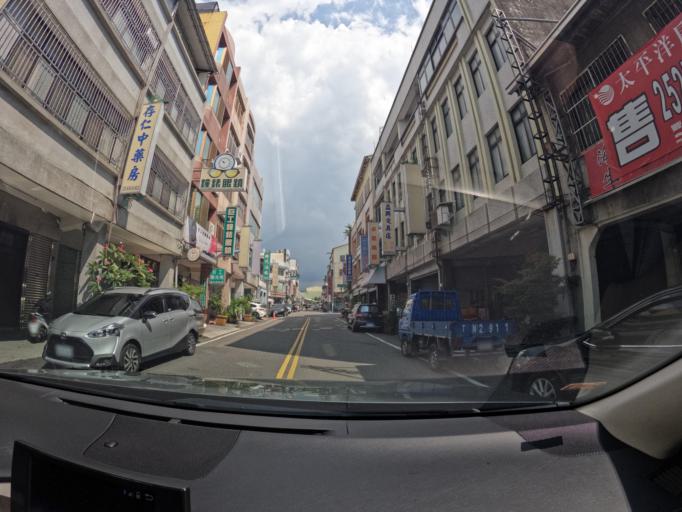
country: TW
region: Taiwan
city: Fengyuan
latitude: 24.3113
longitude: 120.8272
